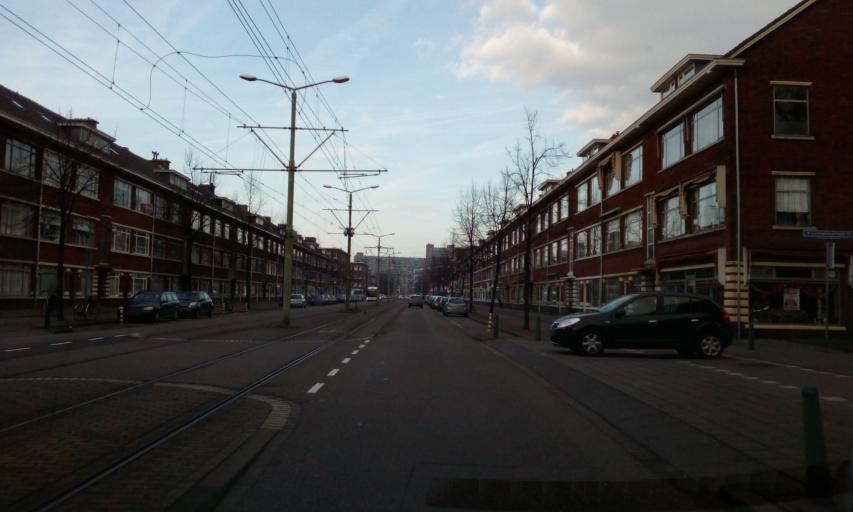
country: NL
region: South Holland
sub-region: Gemeente Rijswijk
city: Rijswijk
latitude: 52.0568
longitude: 4.3233
